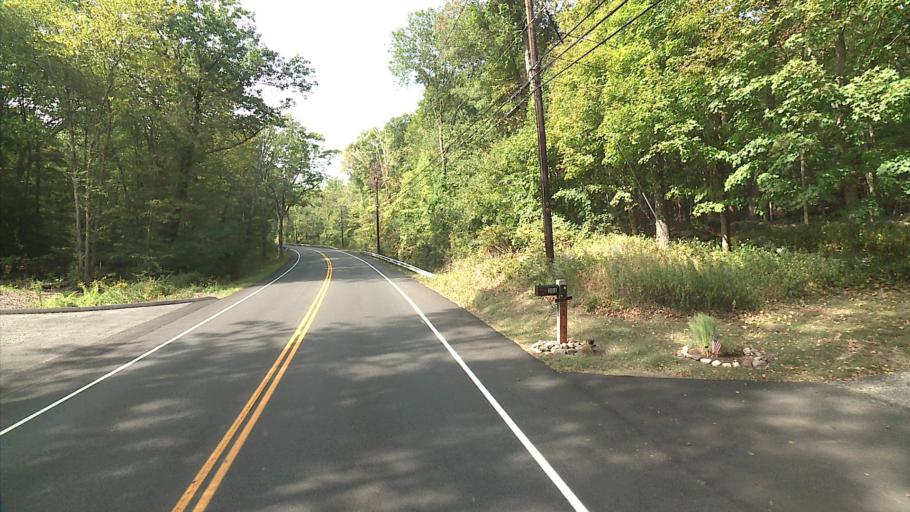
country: US
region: Connecticut
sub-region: New Haven County
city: Oxford
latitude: 41.3891
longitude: -73.1987
